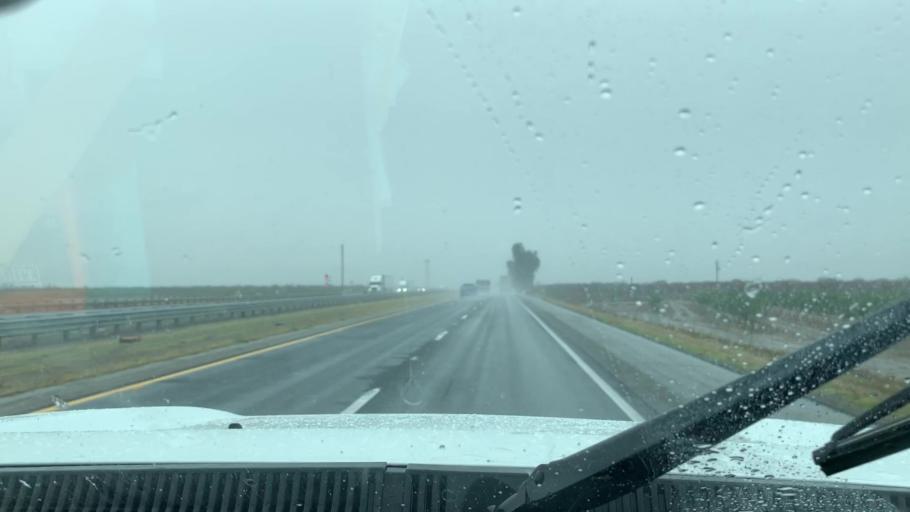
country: US
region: California
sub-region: Tulare County
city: Earlimart
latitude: 35.8533
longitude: -119.2669
